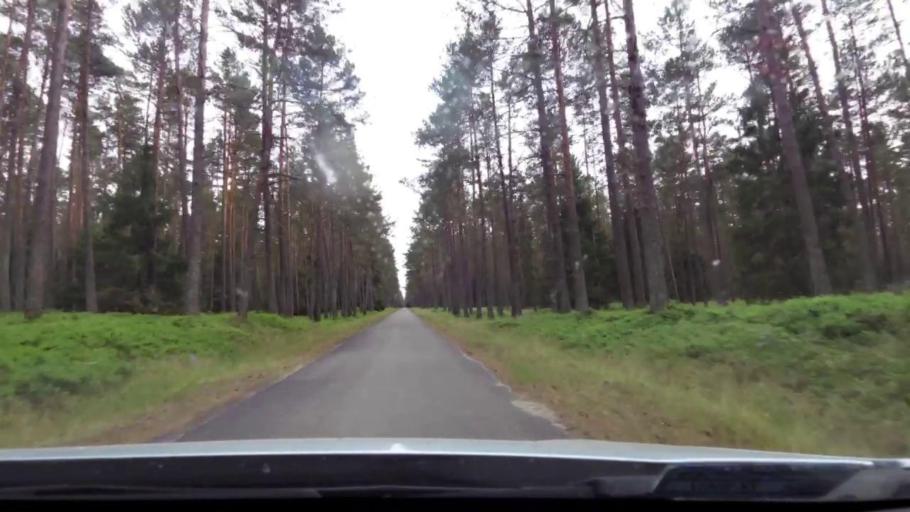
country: PL
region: Pomeranian Voivodeship
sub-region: Powiat bytowski
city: Trzebielino
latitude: 54.2213
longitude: 17.0027
